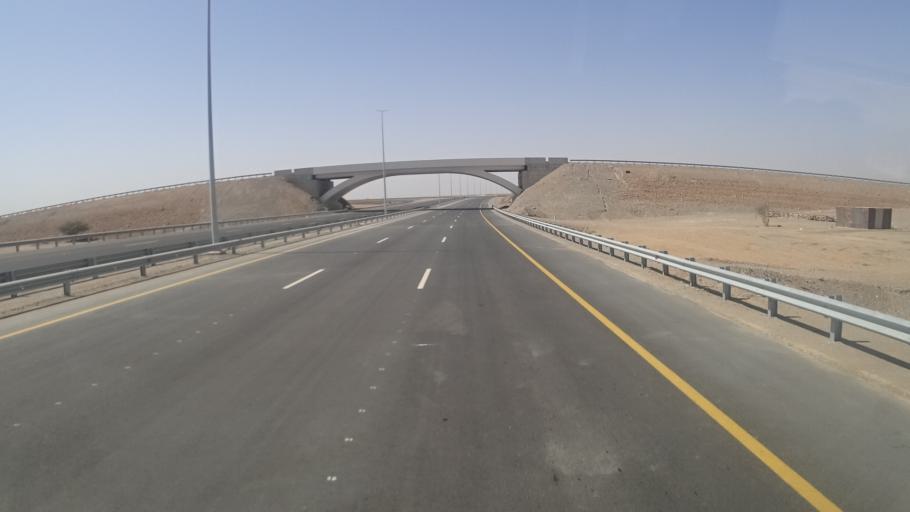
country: OM
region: Ash Sharqiyah
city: Sur
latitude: 22.2802
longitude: 59.2667
